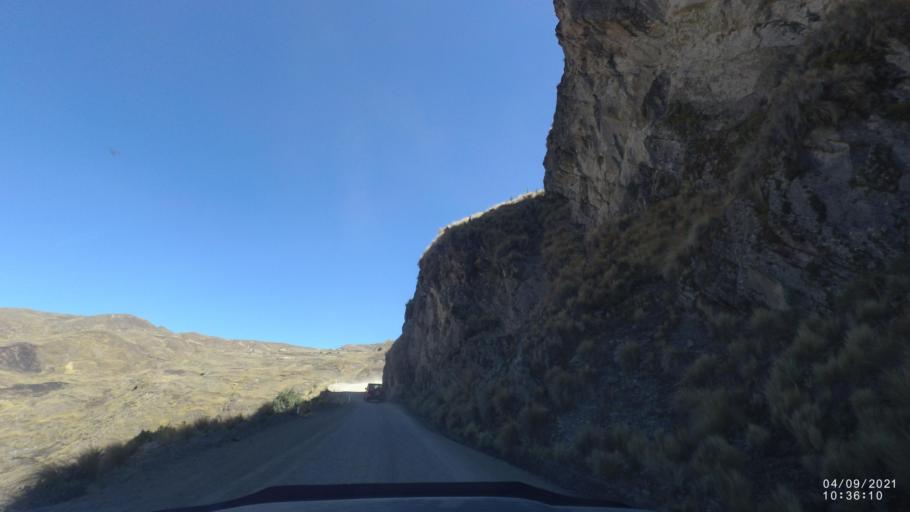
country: BO
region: Cochabamba
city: Sipe Sipe
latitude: -17.2899
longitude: -66.4505
